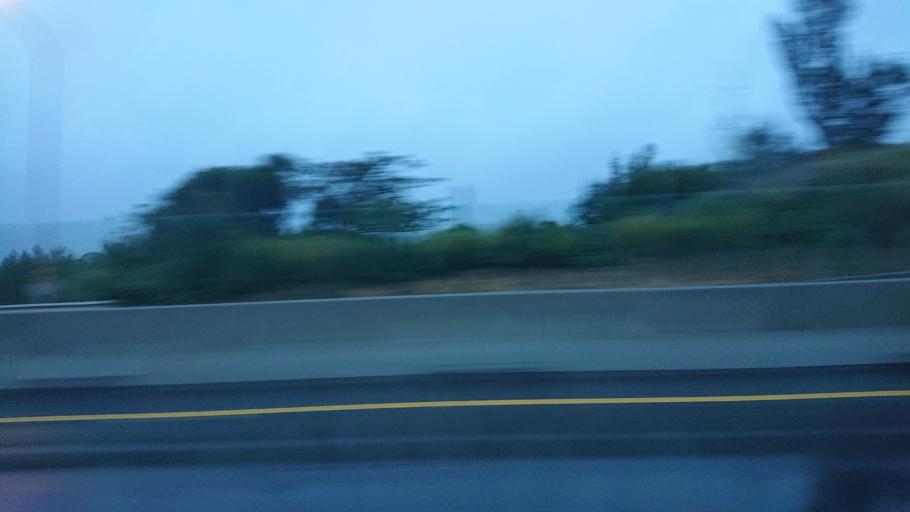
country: TW
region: Taiwan
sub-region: Miaoli
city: Miaoli
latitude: 24.5640
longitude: 120.7145
